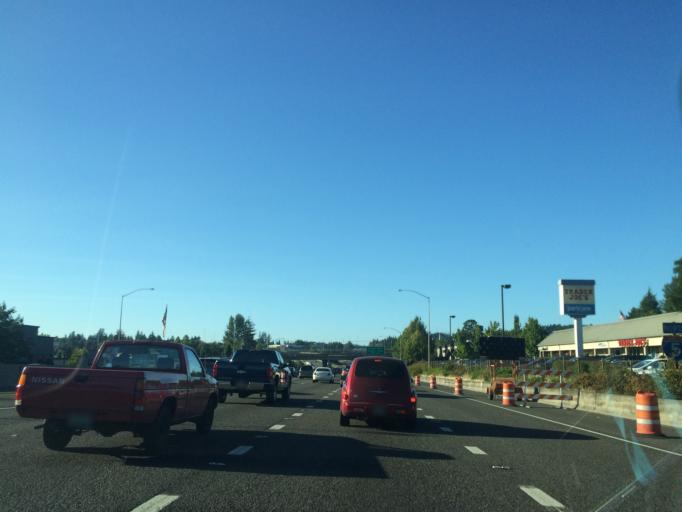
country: US
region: Oregon
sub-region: Washington County
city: Durham
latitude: 45.4132
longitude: -122.7438
